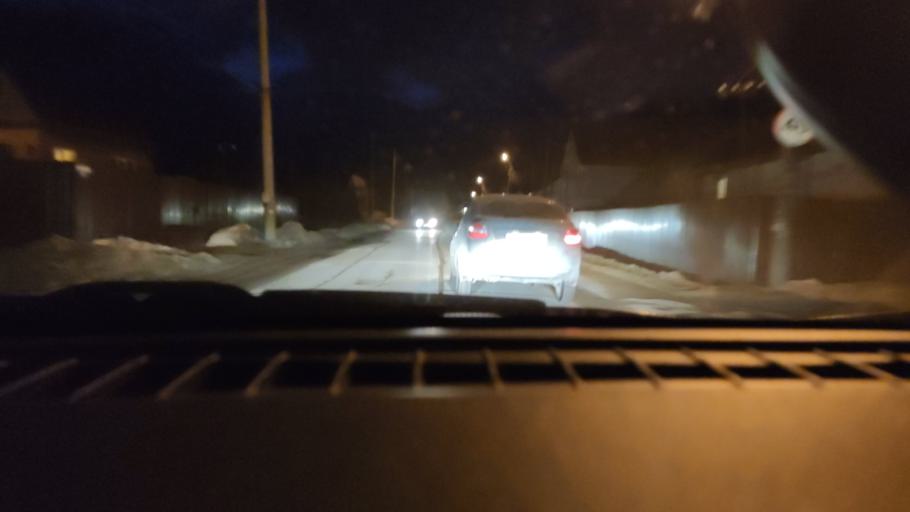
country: RU
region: Perm
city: Overyata
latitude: 58.0880
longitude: 55.8612
